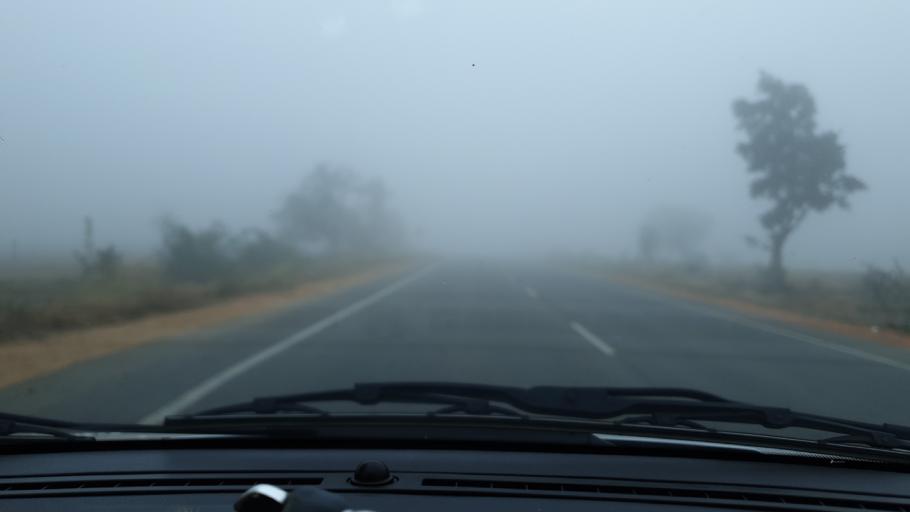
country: IN
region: Telangana
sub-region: Mahbubnagar
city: Nagar Karnul
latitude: 16.6770
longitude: 78.5287
